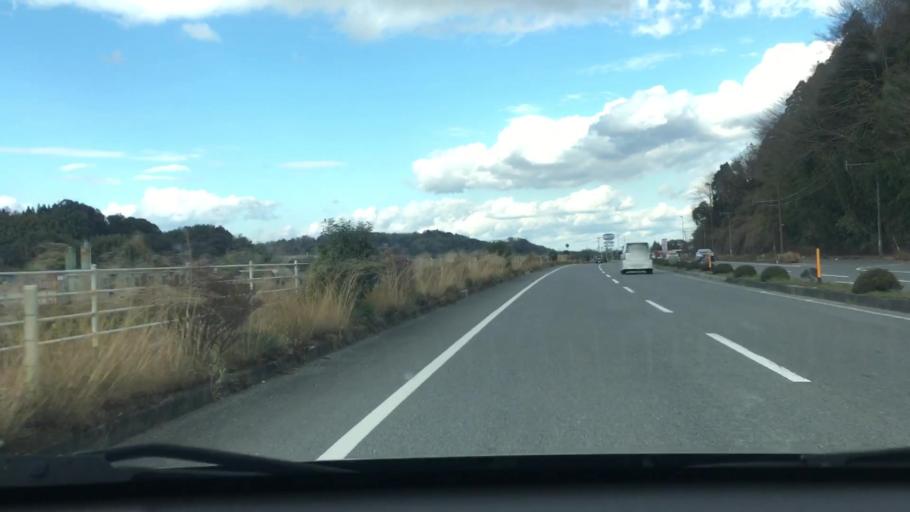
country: JP
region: Oita
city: Oita
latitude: 33.1204
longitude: 131.6537
